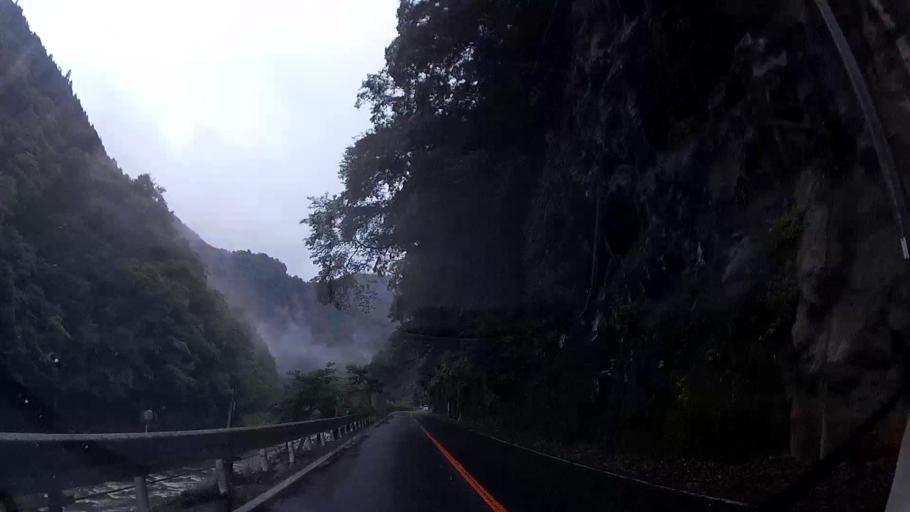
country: JP
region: Oita
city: Hita
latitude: 33.1815
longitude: 131.0201
